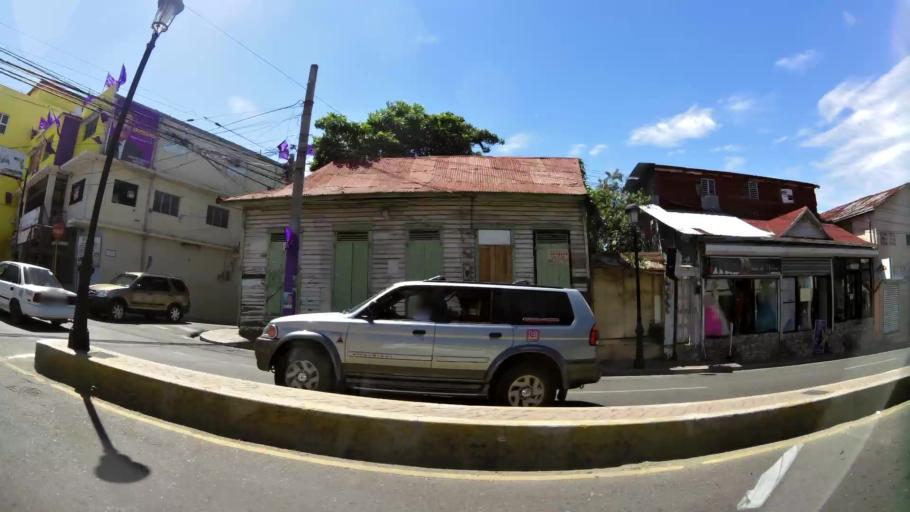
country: DO
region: Santiago
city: Santiago de los Caballeros
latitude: 19.4544
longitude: -70.7075
